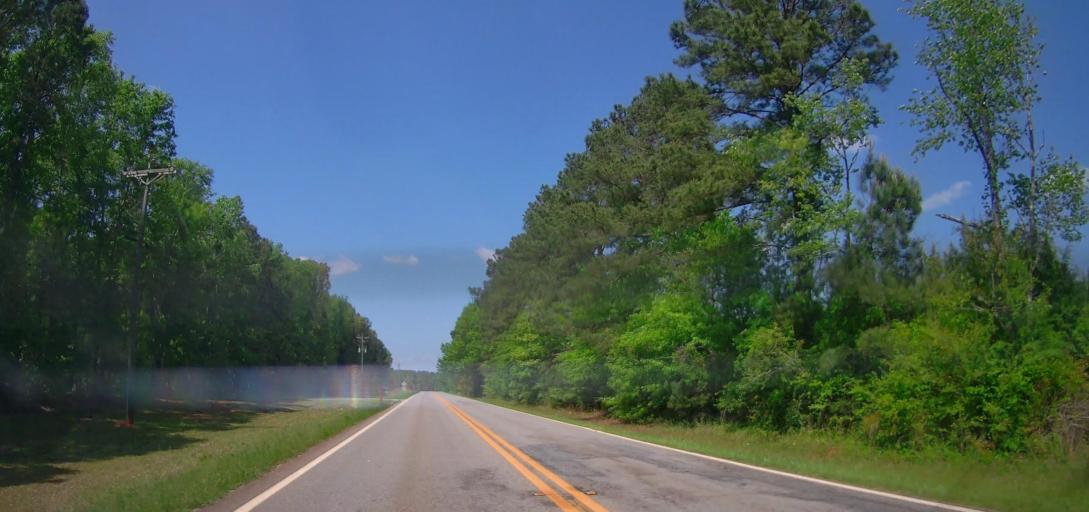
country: US
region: Georgia
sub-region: Putnam County
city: Eatonton
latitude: 33.3083
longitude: -83.3006
